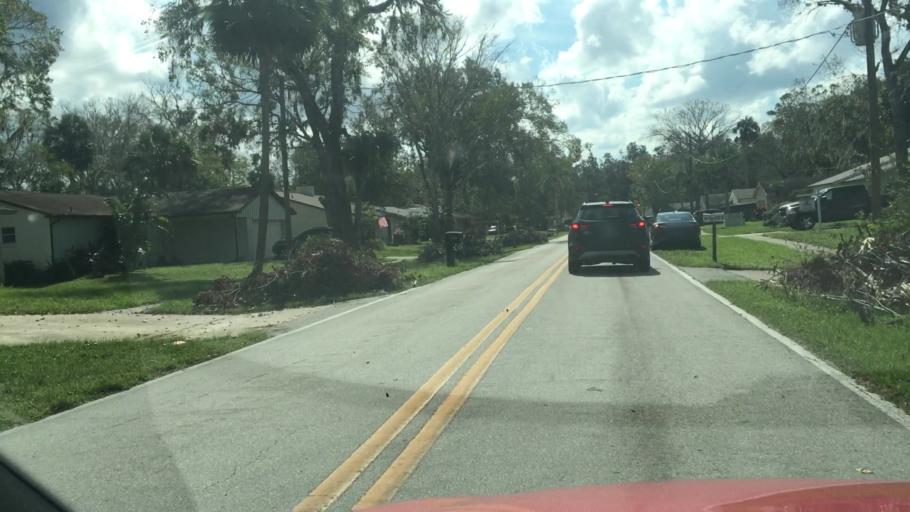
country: US
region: Florida
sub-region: Volusia County
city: Ormond Beach
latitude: 29.2574
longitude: -81.0657
